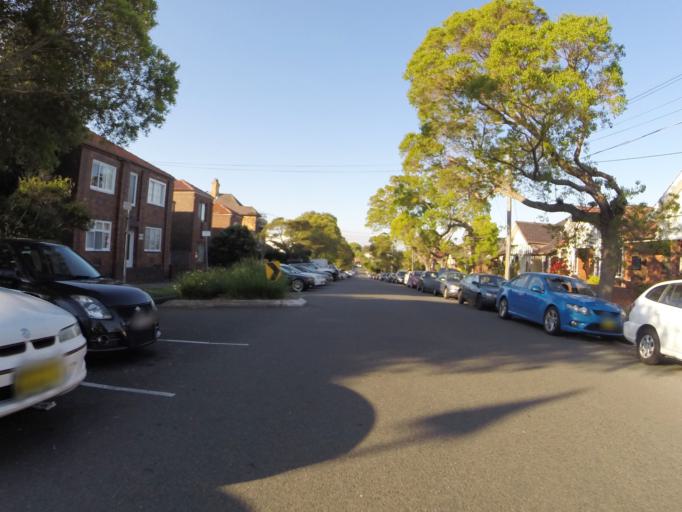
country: AU
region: New South Wales
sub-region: Marrickville
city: Marrickville
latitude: -33.9095
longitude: 151.1562
